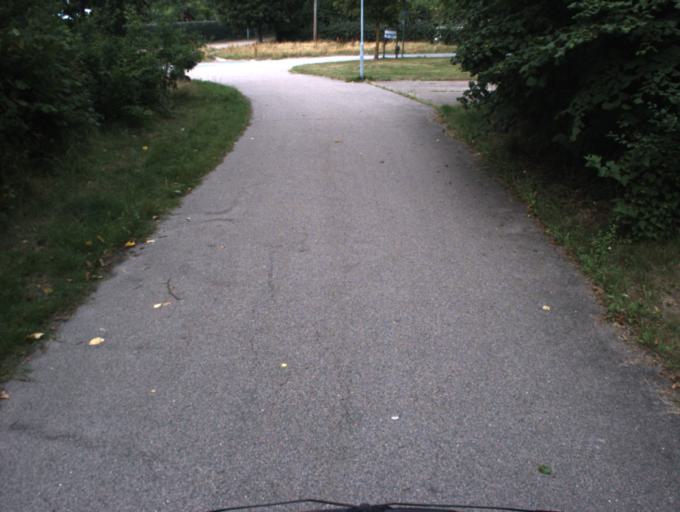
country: SE
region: Skane
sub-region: Helsingborg
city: Helsingborg
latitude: 56.0553
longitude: 12.7306
